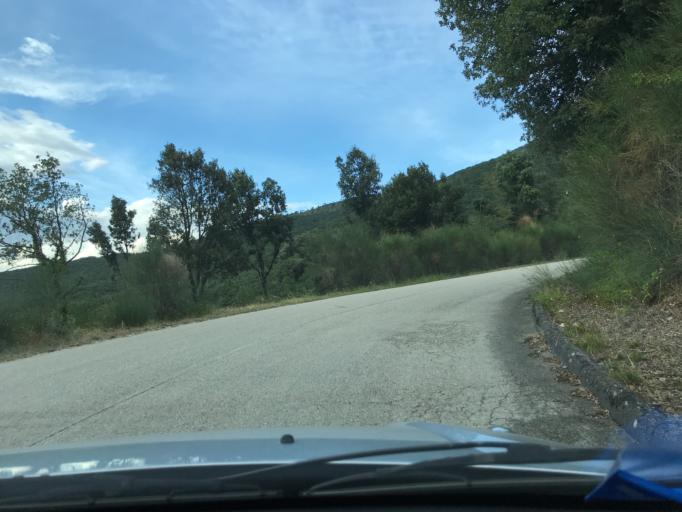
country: IT
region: Umbria
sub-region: Provincia di Terni
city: Montecchio
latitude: 42.6805
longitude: 12.2967
